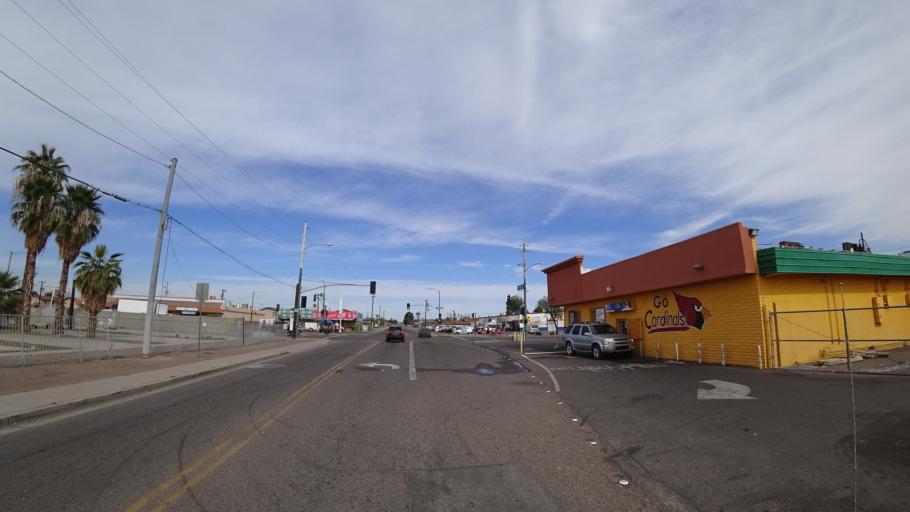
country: US
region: Arizona
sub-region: Maricopa County
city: Phoenix
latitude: 33.4508
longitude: -112.1261
